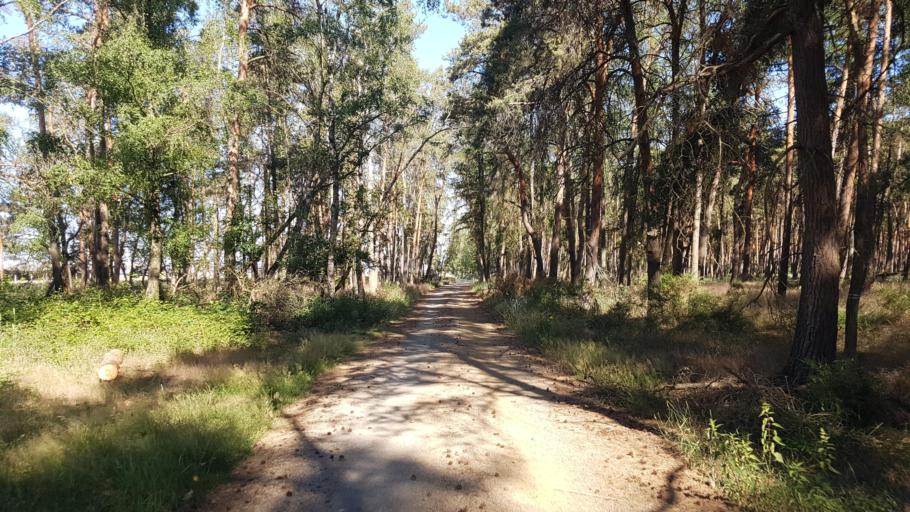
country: DE
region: Brandenburg
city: Juterbog
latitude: 51.9523
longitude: 13.1898
